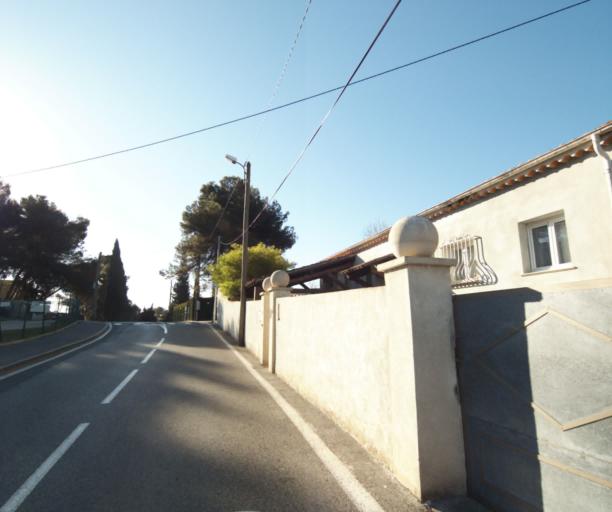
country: FR
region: Provence-Alpes-Cote d'Azur
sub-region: Departement des Alpes-Maritimes
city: Vallauris
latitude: 43.5979
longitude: 7.0759
